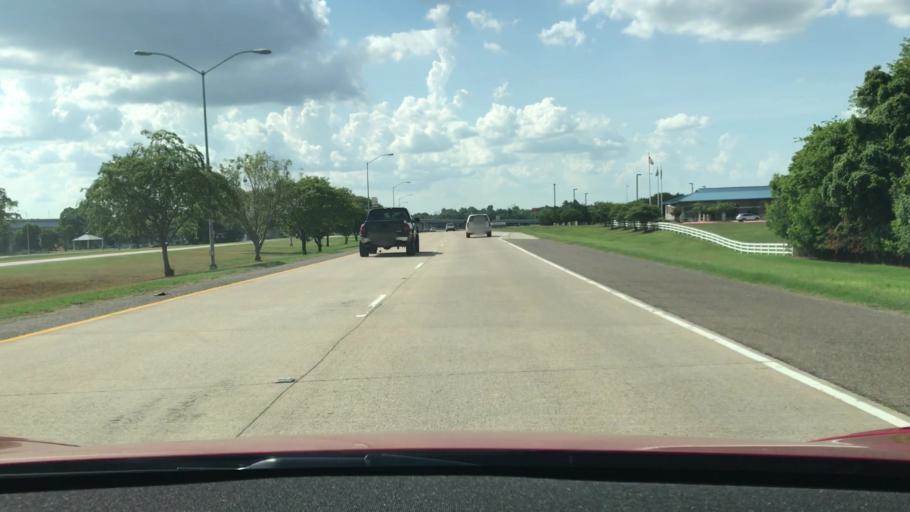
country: US
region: Louisiana
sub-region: Bossier Parish
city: Bossier City
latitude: 32.4904
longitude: -93.6918
